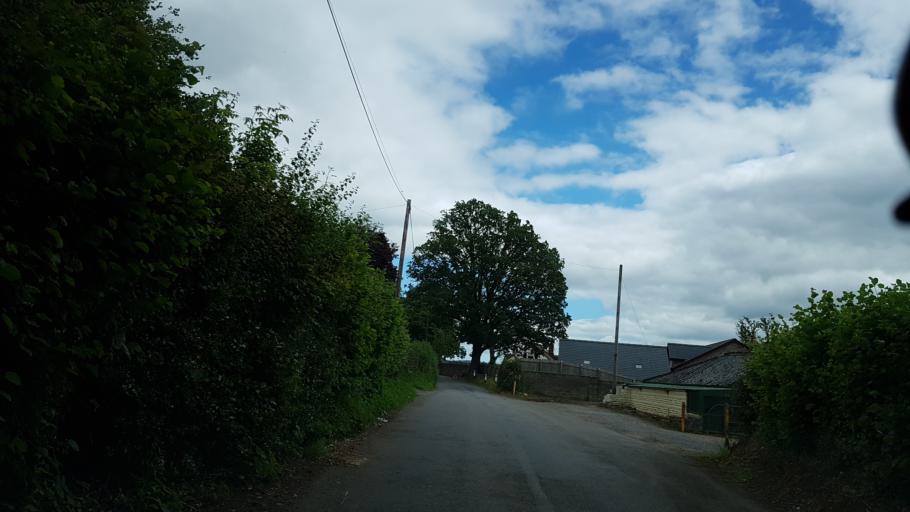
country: GB
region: Wales
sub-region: Monmouthshire
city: Llanarth
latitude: 51.7713
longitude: -2.8372
